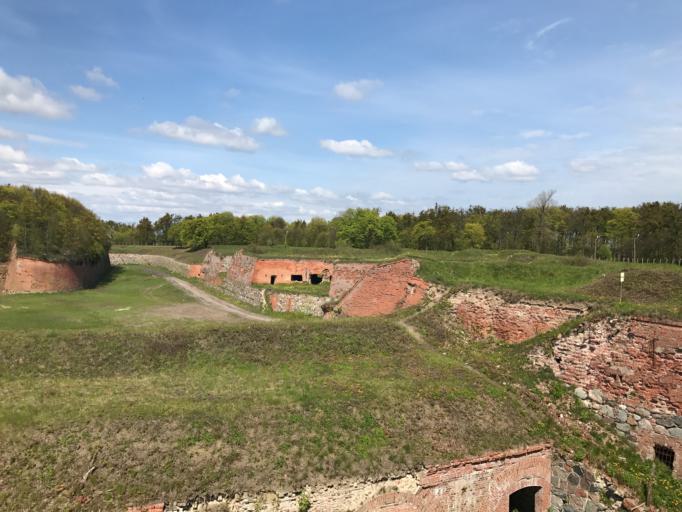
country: PL
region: Kujawsko-Pomorskie
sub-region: Grudziadz
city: Grudziadz
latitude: 53.5135
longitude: 18.7654
